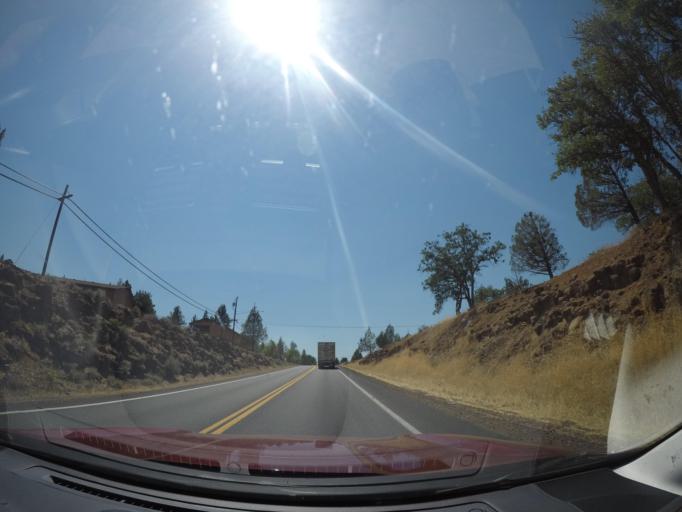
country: US
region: California
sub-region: Shasta County
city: Burney
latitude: 41.0021
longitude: -121.4443
